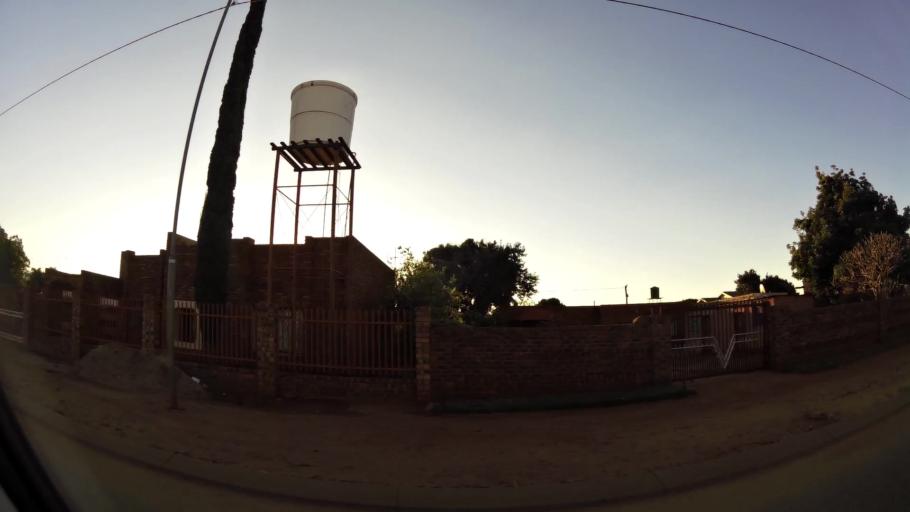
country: ZA
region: Limpopo
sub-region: Waterberg District Municipality
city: Mokopane
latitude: -24.1414
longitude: 28.9949
